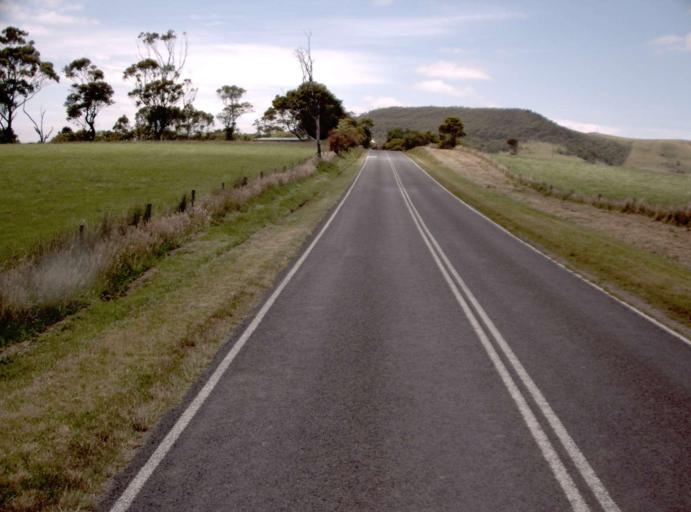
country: AU
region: Victoria
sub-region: Bass Coast
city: North Wonthaggi
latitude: -38.7126
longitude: 146.0943
